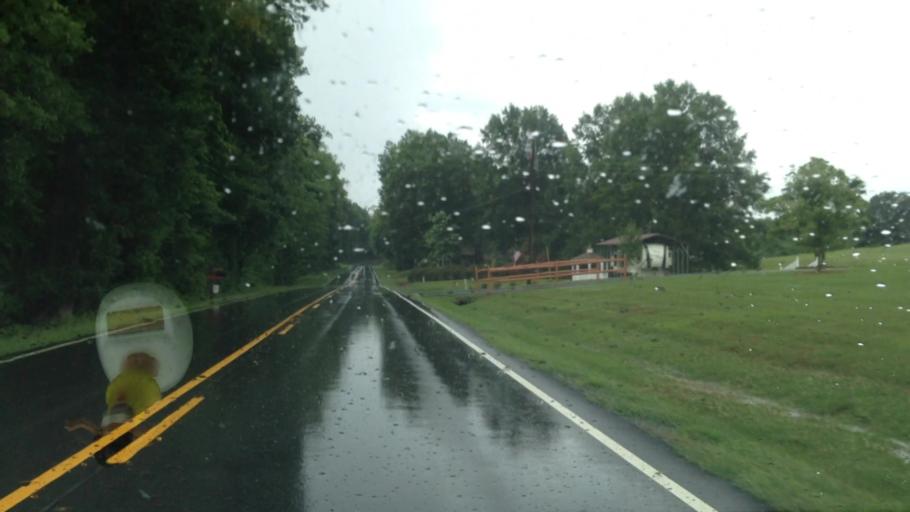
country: US
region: North Carolina
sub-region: Stokes County
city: Danbury
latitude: 36.4446
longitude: -80.1049
